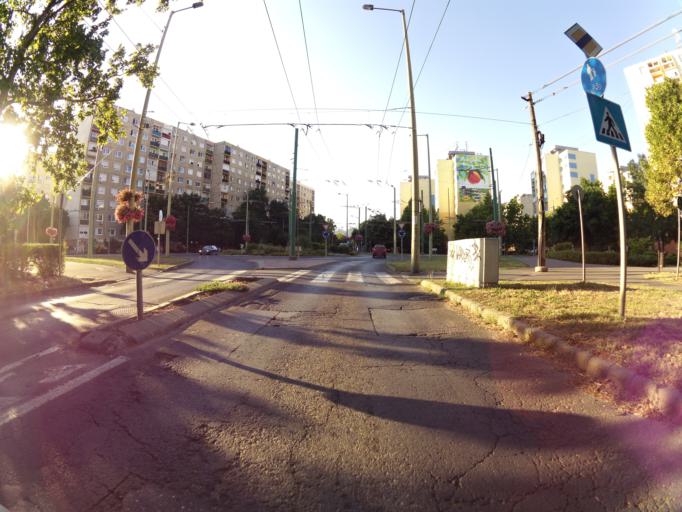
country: HU
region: Csongrad
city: Szeged
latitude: 46.2662
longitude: 20.1676
